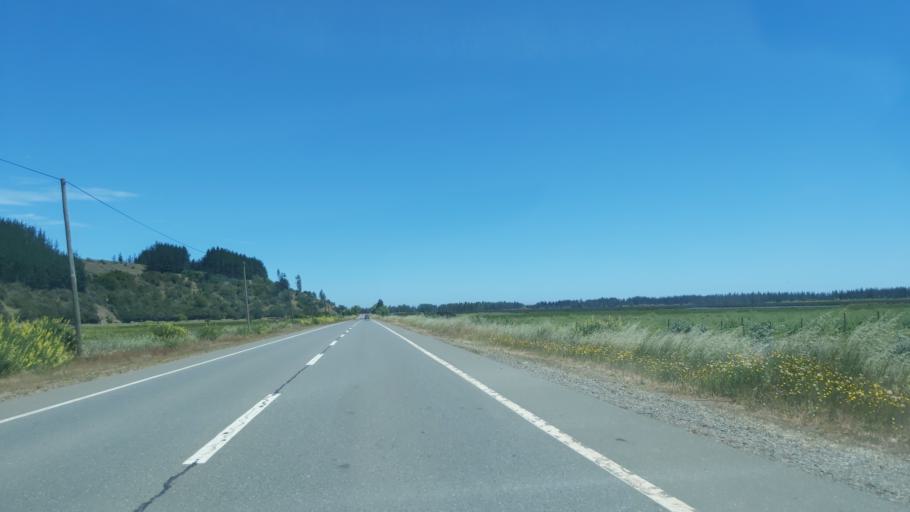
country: CL
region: Maule
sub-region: Provincia de Talca
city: Constitucion
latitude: -35.1547
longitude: -72.2326
